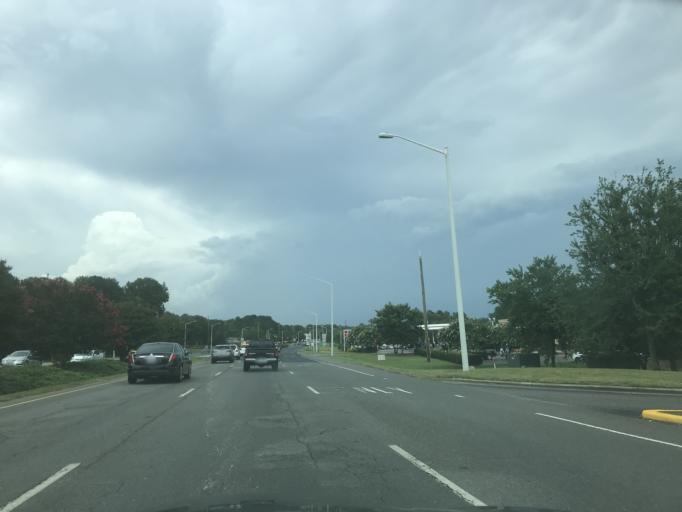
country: US
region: North Carolina
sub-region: Johnston County
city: Clayton
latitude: 35.6558
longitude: -78.4765
